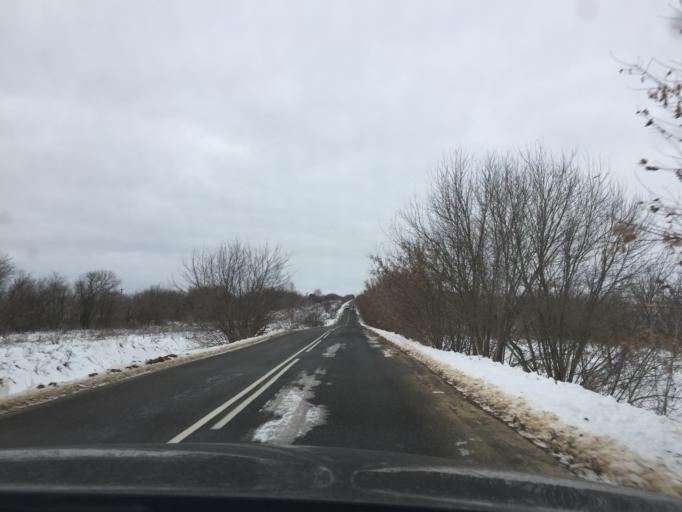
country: RU
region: Tula
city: Teploye
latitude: 53.7906
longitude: 37.6099
